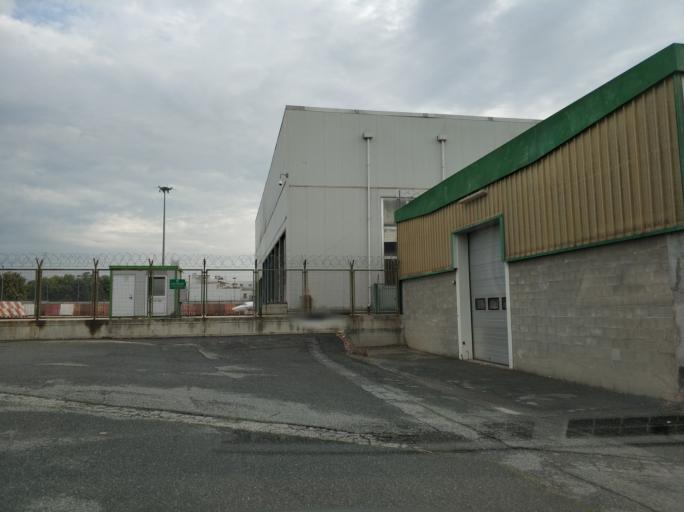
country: IT
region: Piedmont
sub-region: Provincia di Torino
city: Caselle Torinese
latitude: 45.1963
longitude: 7.6422
